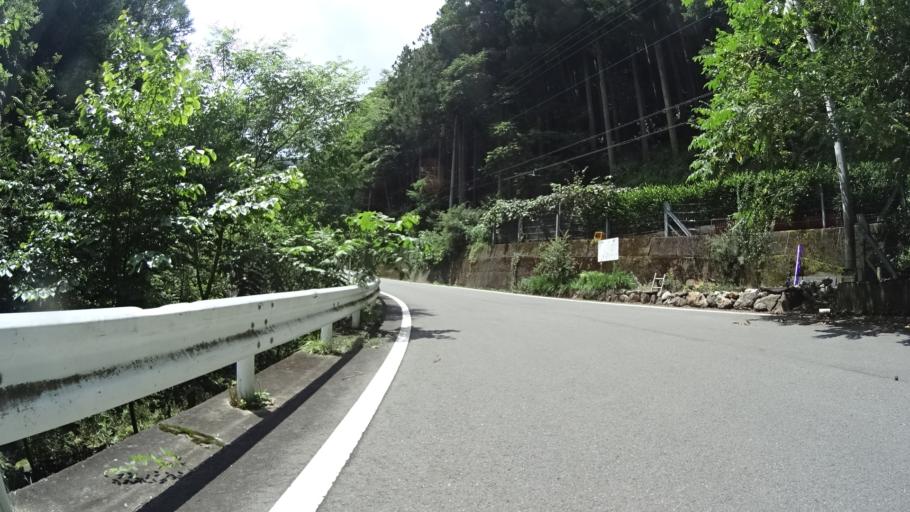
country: JP
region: Nagano
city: Saku
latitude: 36.0711
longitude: 138.7018
